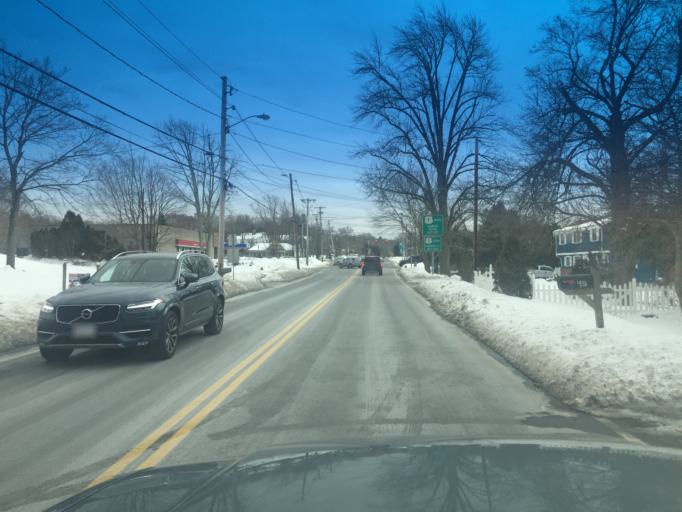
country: US
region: Massachusetts
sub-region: Norfolk County
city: Walpole
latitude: 42.1034
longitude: -71.2599
